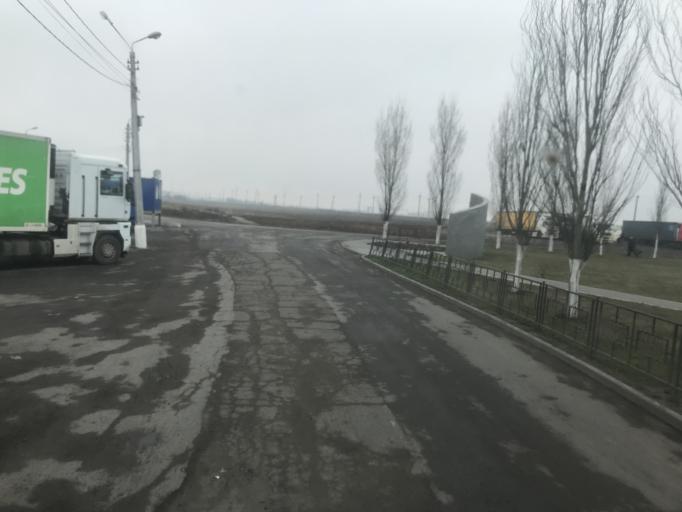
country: RU
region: Volgograd
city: Svetlyy Yar
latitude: 48.4906
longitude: 44.6619
